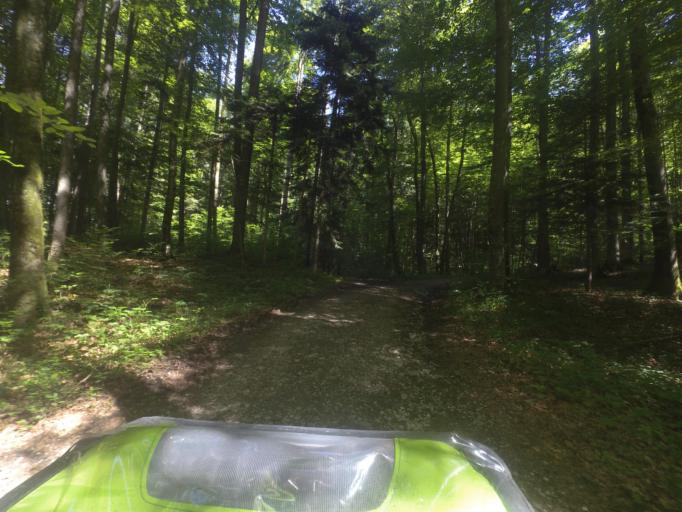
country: AT
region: Salzburg
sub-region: Politischer Bezirk Hallein
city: Puch bei Hallein
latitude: 47.7142
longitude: 13.1060
